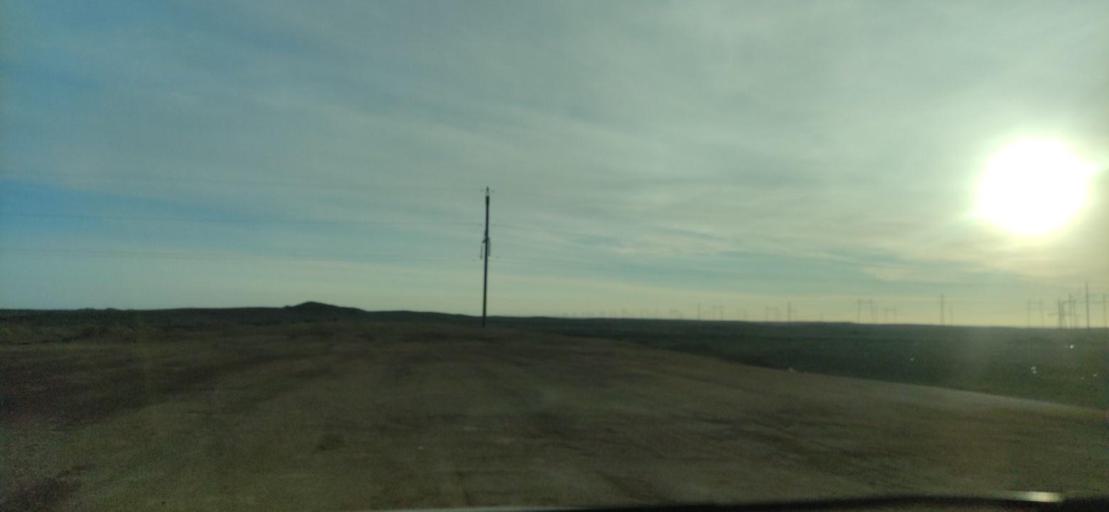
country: KZ
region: Qaraghandy
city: Saryshaghan
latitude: 46.1215
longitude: 73.5954
